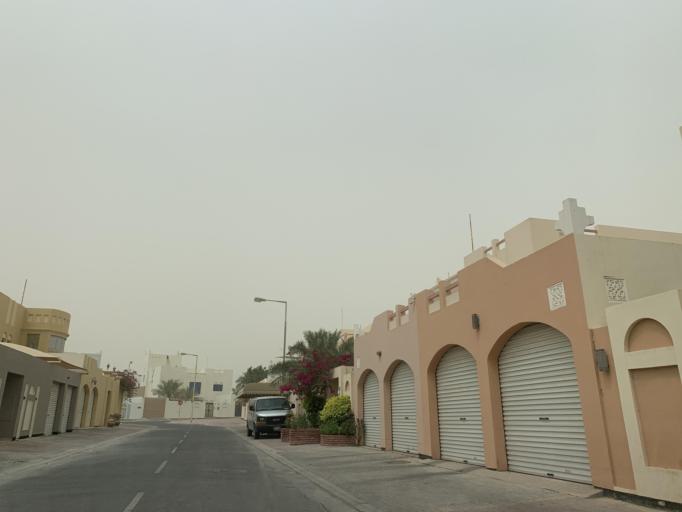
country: BH
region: Central Governorate
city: Madinat Hamad
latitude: 26.1374
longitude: 50.5139
